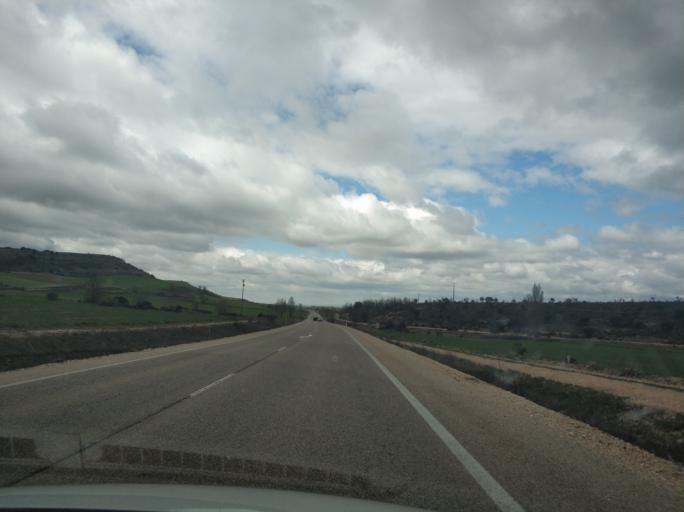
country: ES
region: Castille and Leon
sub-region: Provincia de Burgos
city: Cubillo del Campo
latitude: 42.1497
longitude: -3.5939
